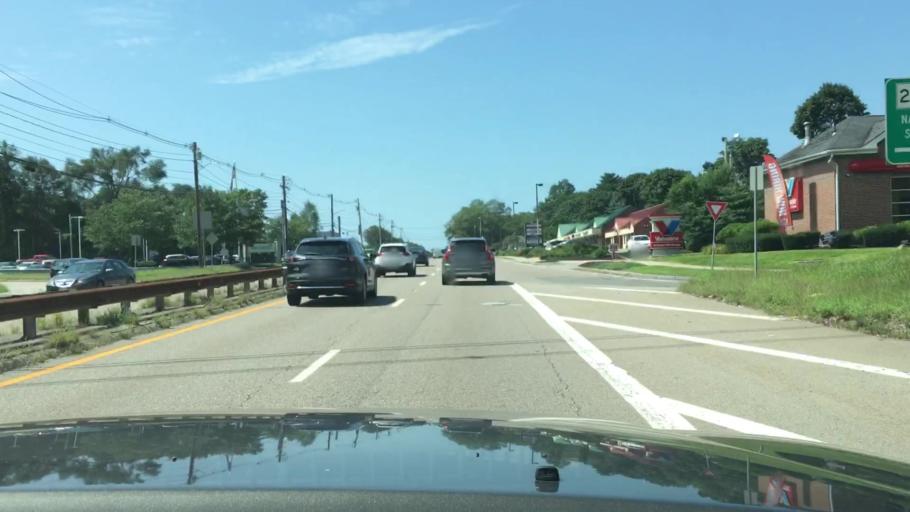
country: US
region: Massachusetts
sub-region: Middlesex County
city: Natick
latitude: 42.3000
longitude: -71.3605
